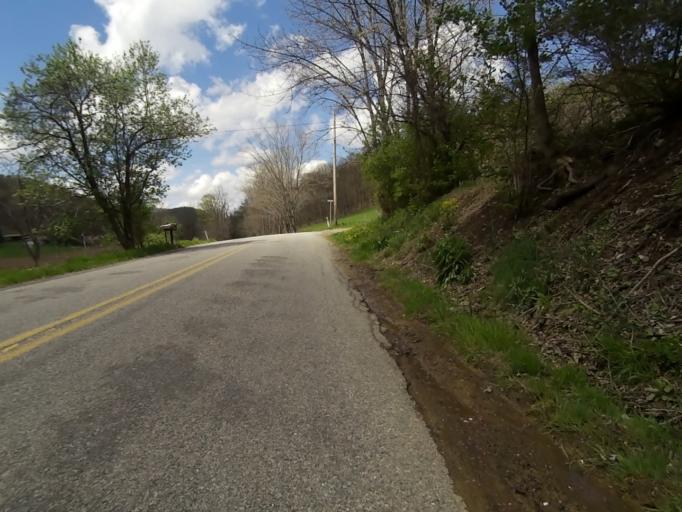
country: US
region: Pennsylvania
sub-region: Centre County
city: Milesburg
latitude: 40.9282
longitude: -77.8728
